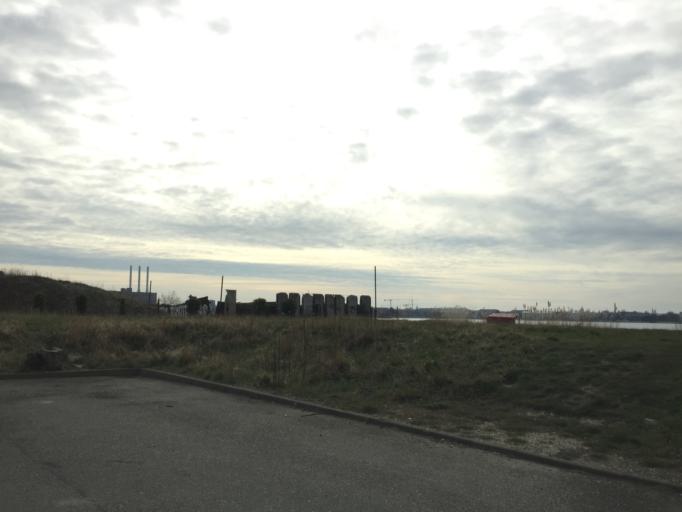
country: DK
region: Capital Region
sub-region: Gentofte Kommune
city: Charlottenlund
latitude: 55.7226
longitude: 12.6019
